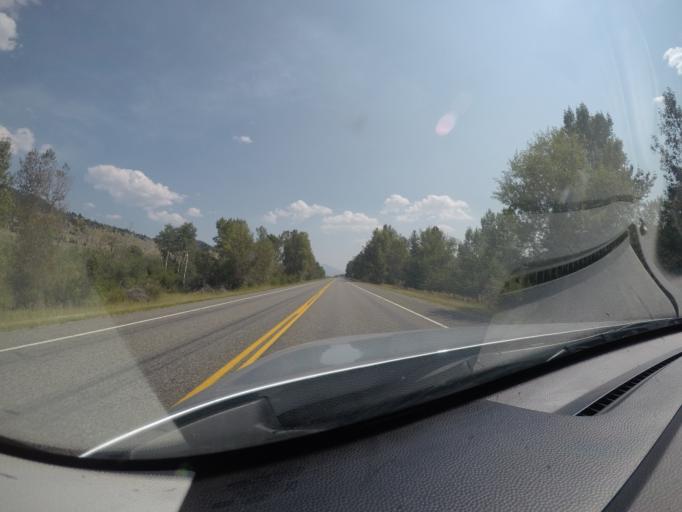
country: US
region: Montana
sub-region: Gallatin County
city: Big Sky
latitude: 44.8936
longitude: -111.5828
